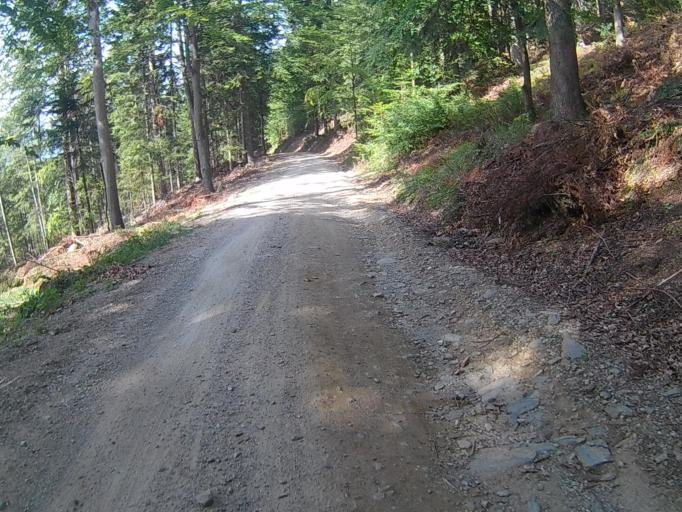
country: SI
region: Ruse
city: Bistrica ob Dravi
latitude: 46.5148
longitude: 15.5523
